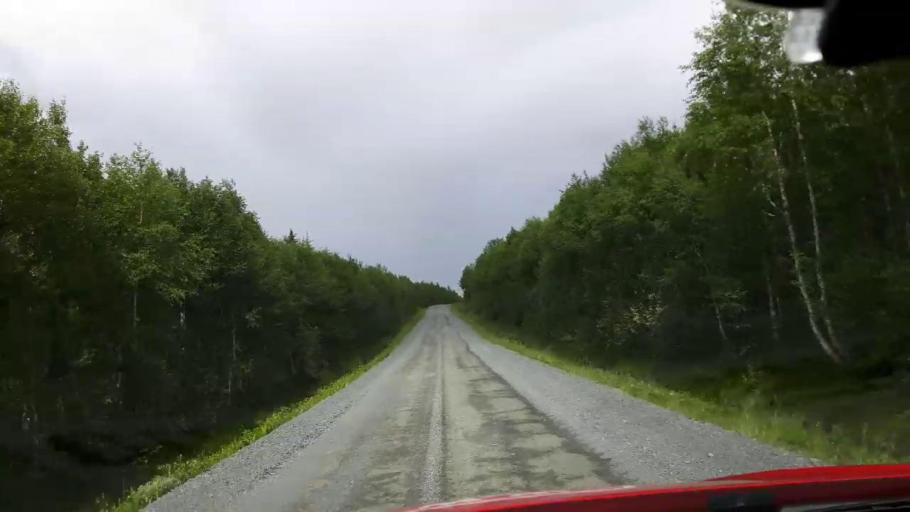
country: NO
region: Nord-Trondelag
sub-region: Lierne
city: Sandvika
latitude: 64.1522
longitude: 13.9814
